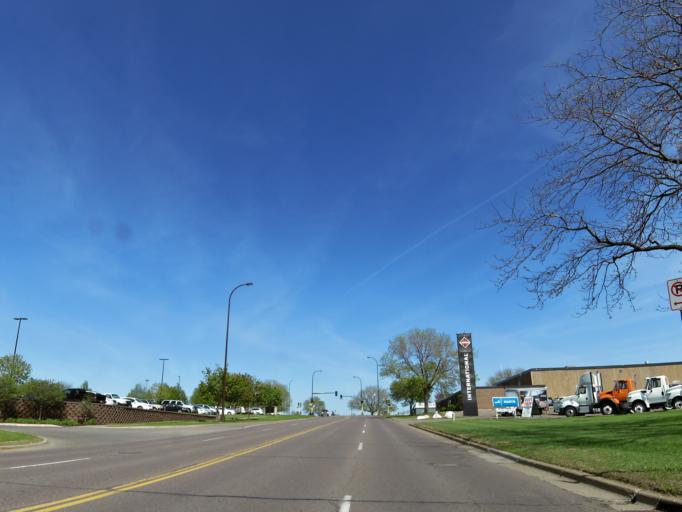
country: US
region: Minnesota
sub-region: Ramsey County
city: Lauderdale
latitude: 44.9987
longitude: -93.2197
